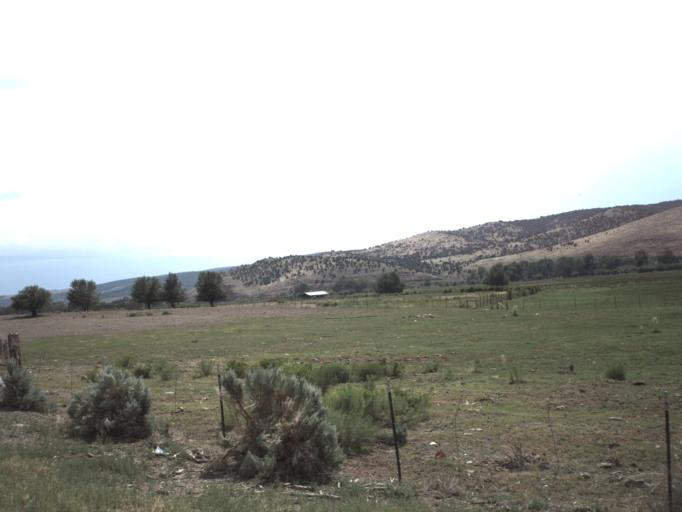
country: US
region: Utah
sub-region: Piute County
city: Junction
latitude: 38.1080
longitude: -111.9871
